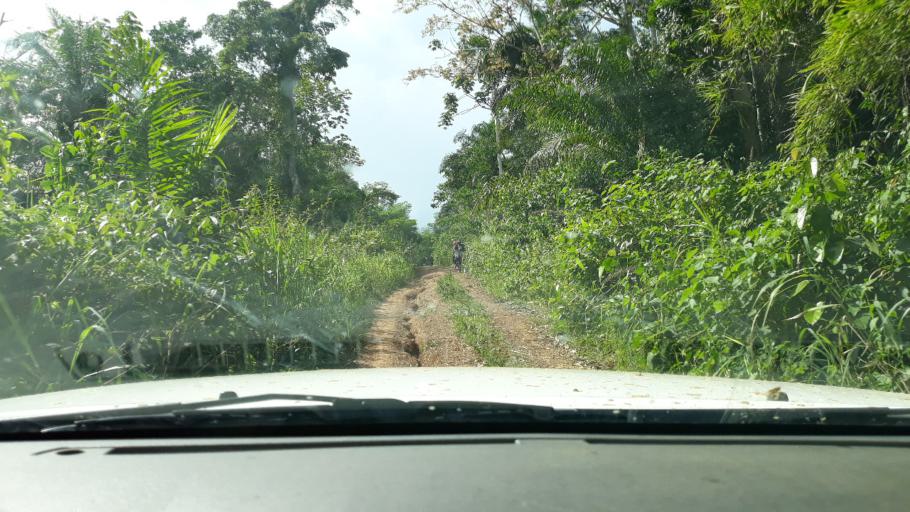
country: CD
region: Maniema
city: Kampene
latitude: -2.7695
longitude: 26.9312
